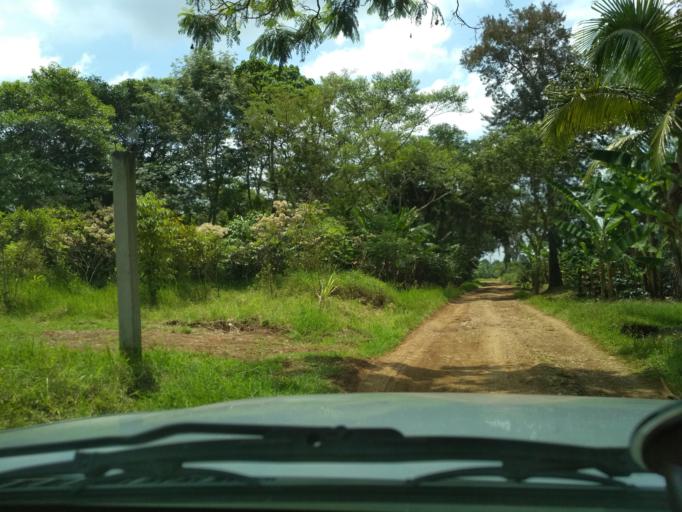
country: MX
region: Veracruz
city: Monte Blanco
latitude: 18.9585
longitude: -97.0176
